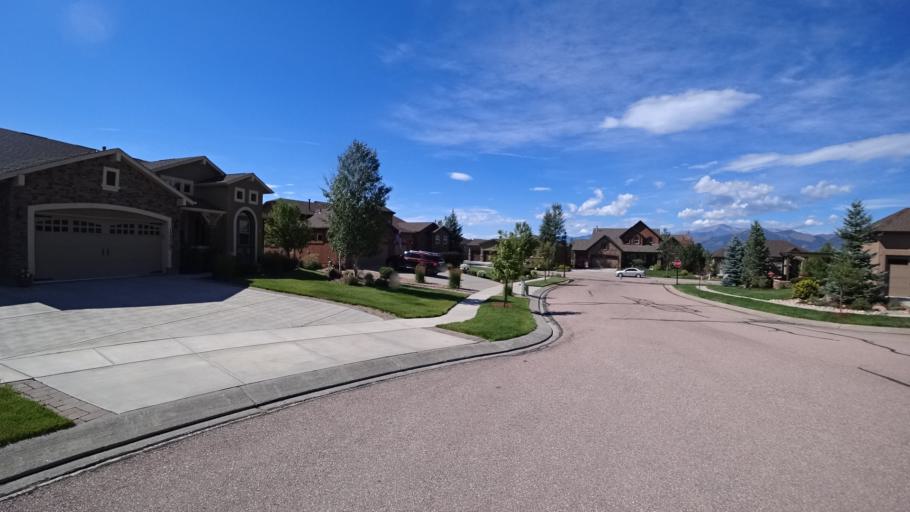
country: US
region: Colorado
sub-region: El Paso County
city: Gleneagle
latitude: 39.0266
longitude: -104.8010
